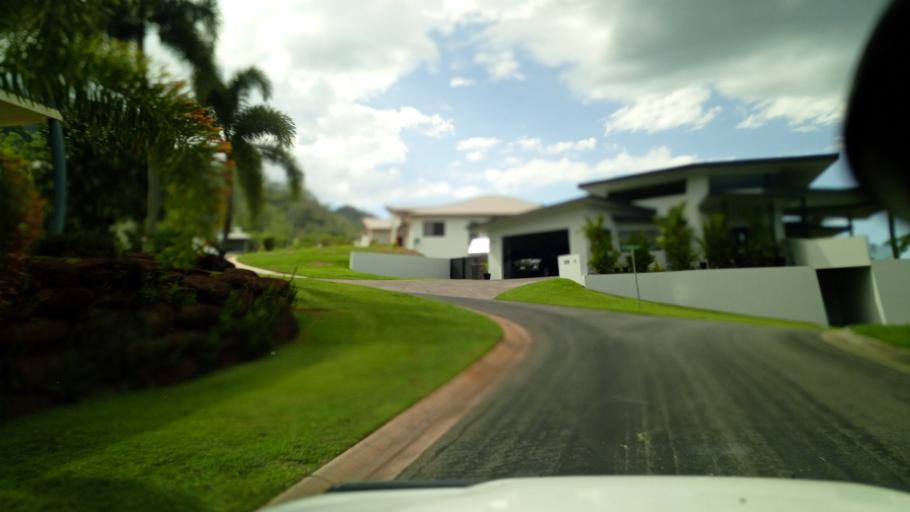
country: AU
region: Queensland
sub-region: Cairns
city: Woree
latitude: -16.9258
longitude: 145.7227
